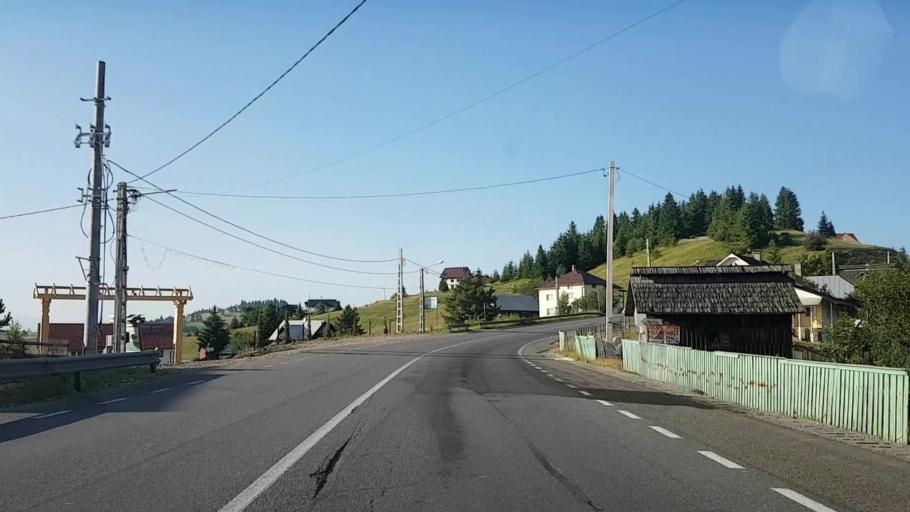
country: RO
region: Bistrita-Nasaud
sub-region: Comuna Lunca Ilvei
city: Lunca Ilvei
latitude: 47.2337
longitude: 24.9979
